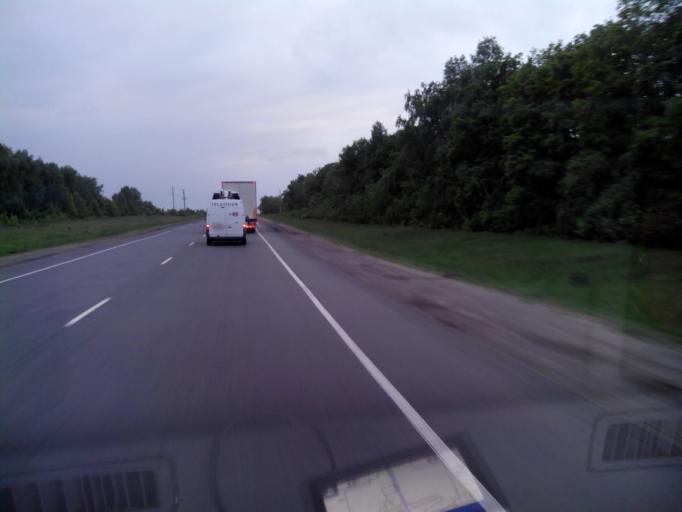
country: RU
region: Penza
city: Chemodanovka
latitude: 53.2225
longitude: 45.3232
